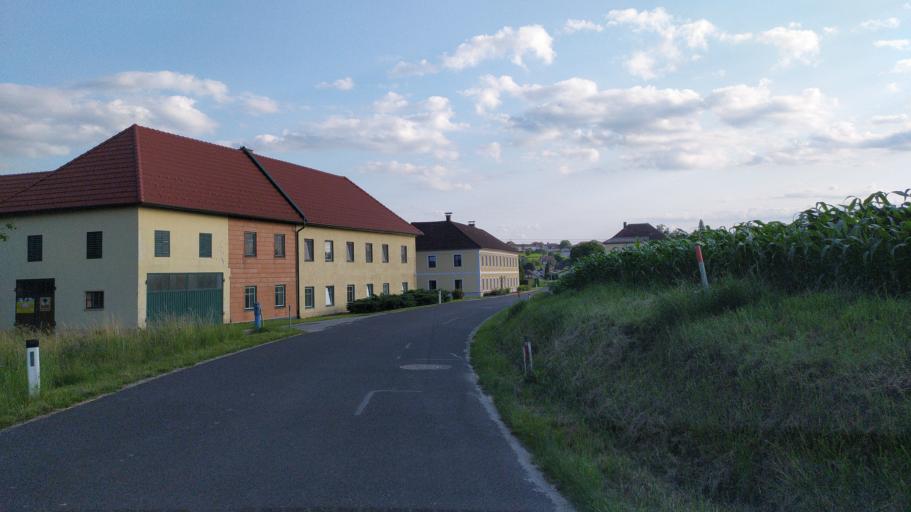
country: AT
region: Lower Austria
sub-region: Politischer Bezirk Amstetten
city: Strengberg
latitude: 48.1504
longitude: 14.6576
